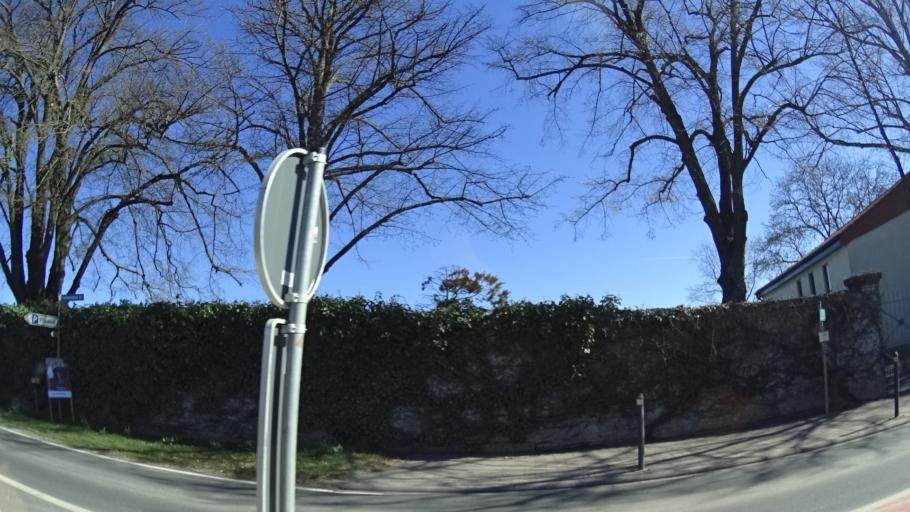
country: DE
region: Rheinland-Pfalz
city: Weinolsheim
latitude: 49.8193
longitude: 8.2703
